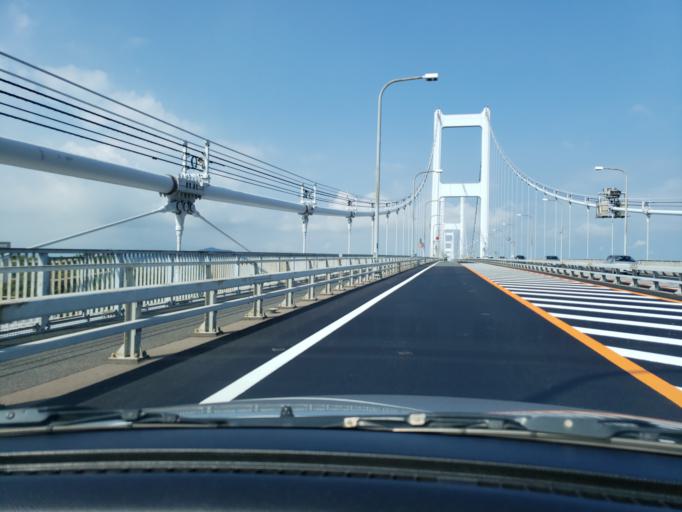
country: JP
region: Hiroshima
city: Innoshima
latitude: 34.1257
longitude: 133.0127
